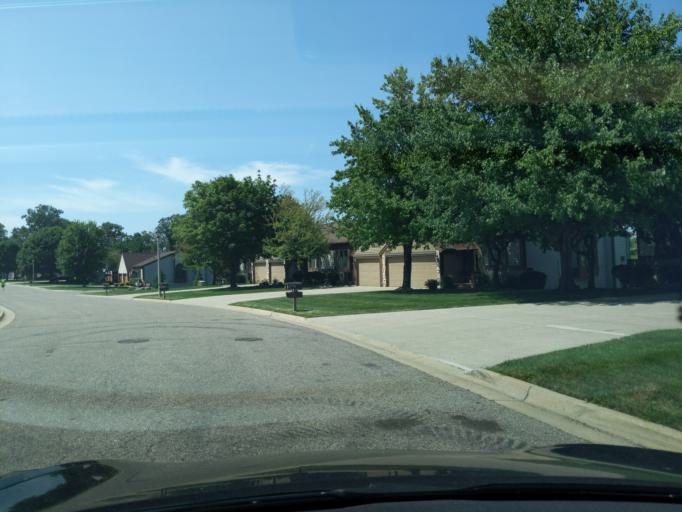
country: US
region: Michigan
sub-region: Eaton County
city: Waverly
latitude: 42.7477
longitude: -84.6480
